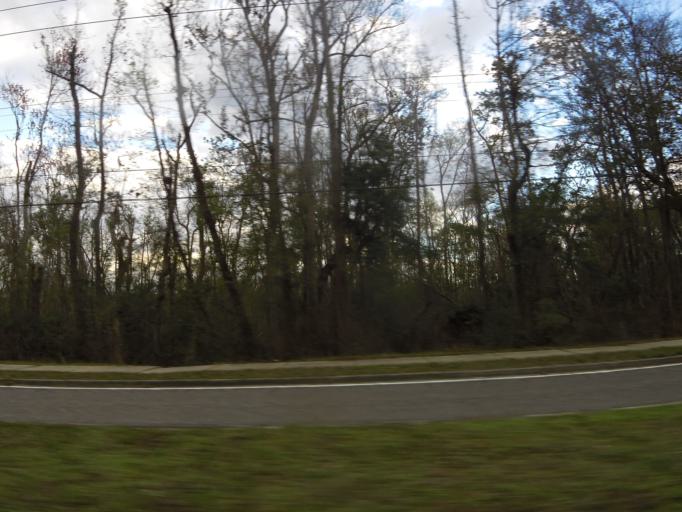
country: US
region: Florida
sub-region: Saint Johns County
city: Fruit Cove
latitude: 30.2115
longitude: -81.5840
